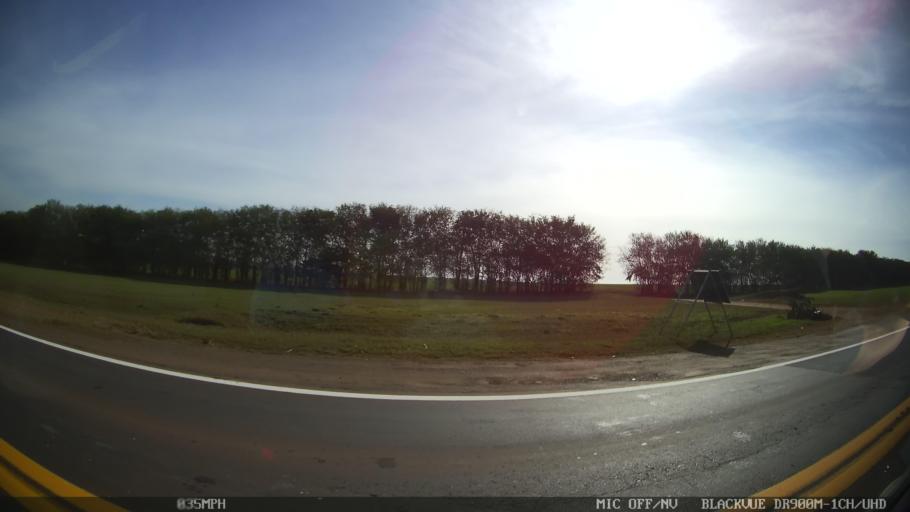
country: BR
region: Sao Paulo
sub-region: Rio Das Pedras
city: Rio das Pedras
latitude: -22.7970
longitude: -47.6075
